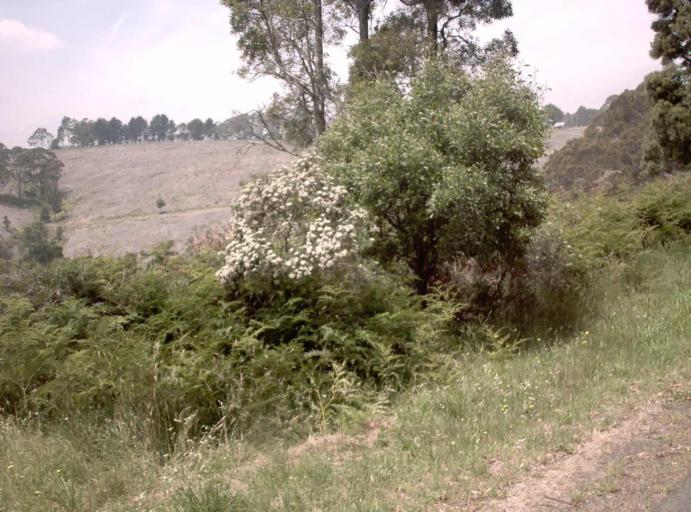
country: AU
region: Victoria
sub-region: Latrobe
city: Traralgon
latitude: -38.3322
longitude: 146.7242
